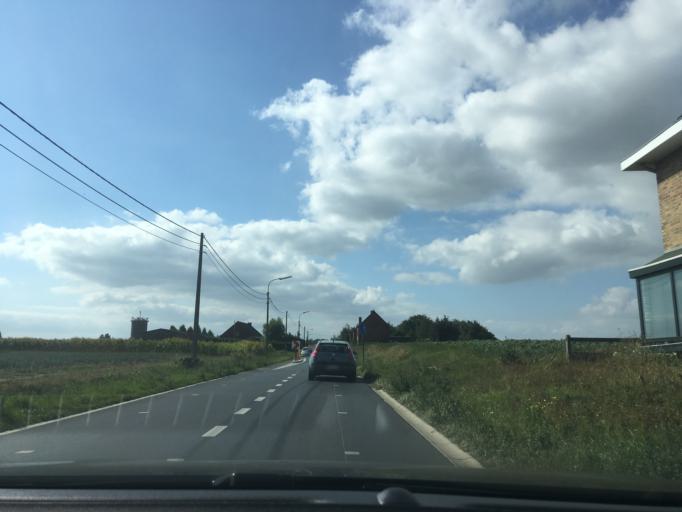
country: BE
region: Flanders
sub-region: Provincie West-Vlaanderen
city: Moorslede
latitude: 50.9120
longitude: 3.0251
